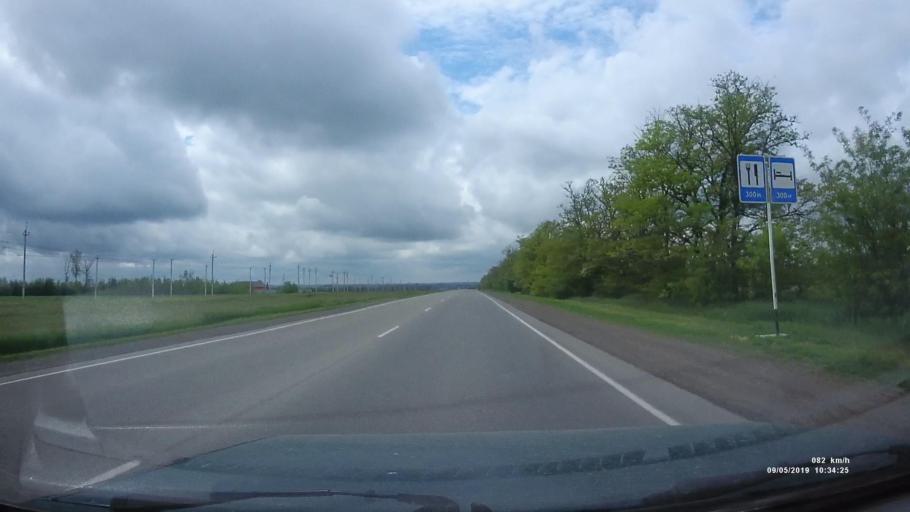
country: RU
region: Rostov
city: Peshkovo
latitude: 47.0543
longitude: 39.4198
